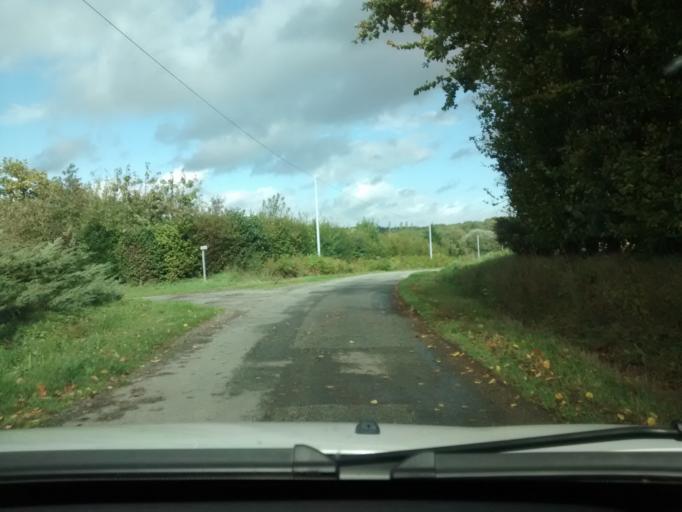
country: FR
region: Brittany
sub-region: Departement d'Ille-et-Vilaine
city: Chateaubourg
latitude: 48.1228
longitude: -1.3869
